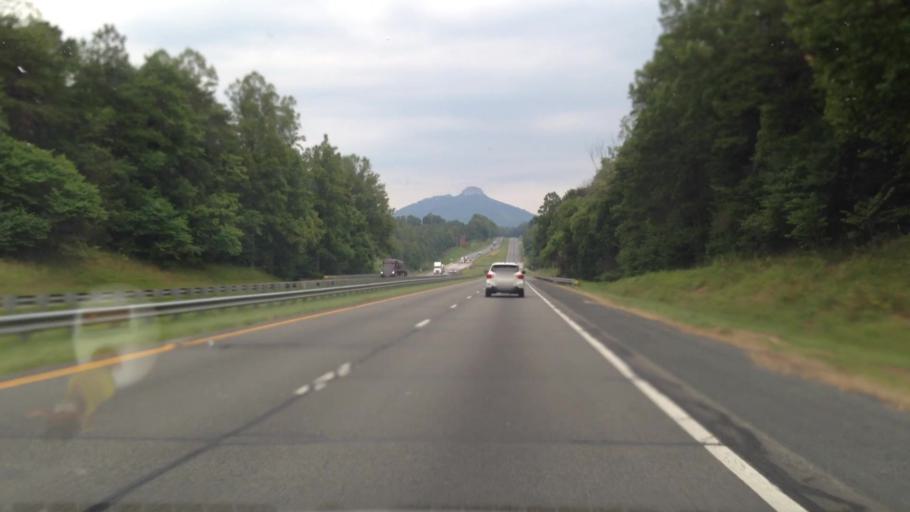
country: US
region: North Carolina
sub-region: Stokes County
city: King
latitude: 36.2982
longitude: -80.4101
